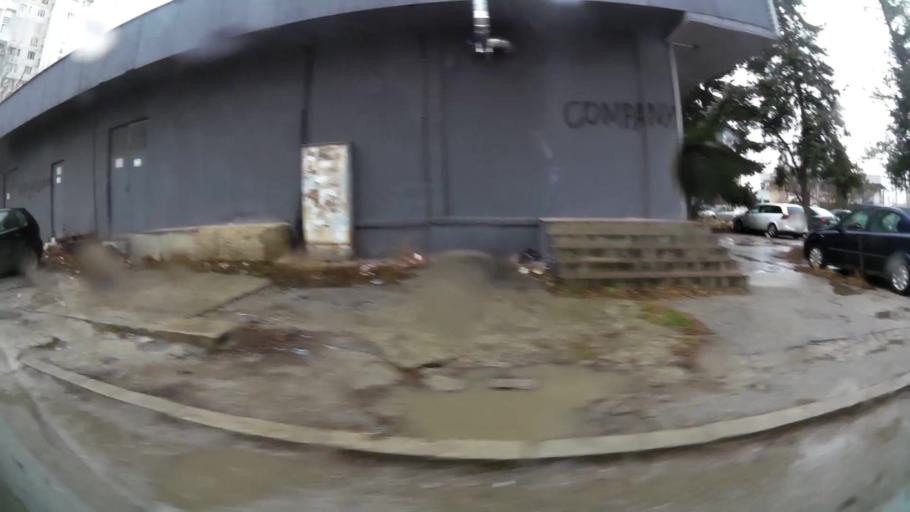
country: BG
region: Sofia-Capital
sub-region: Stolichna Obshtina
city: Sofia
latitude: 42.6536
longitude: 23.3686
